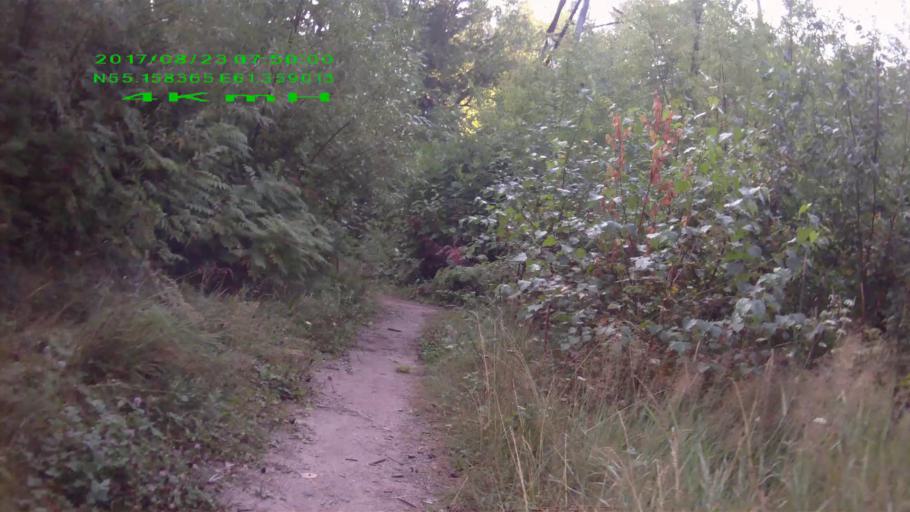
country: RU
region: Chelyabinsk
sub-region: Gorod Chelyabinsk
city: Chelyabinsk
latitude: 55.1583
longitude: 61.3591
